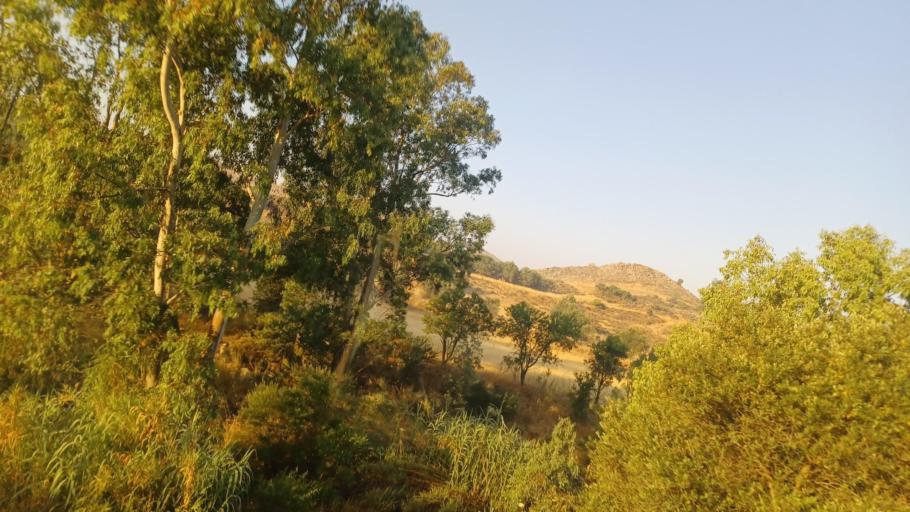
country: CY
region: Larnaka
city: Mosfiloti
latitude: 34.9741
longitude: 33.4224
